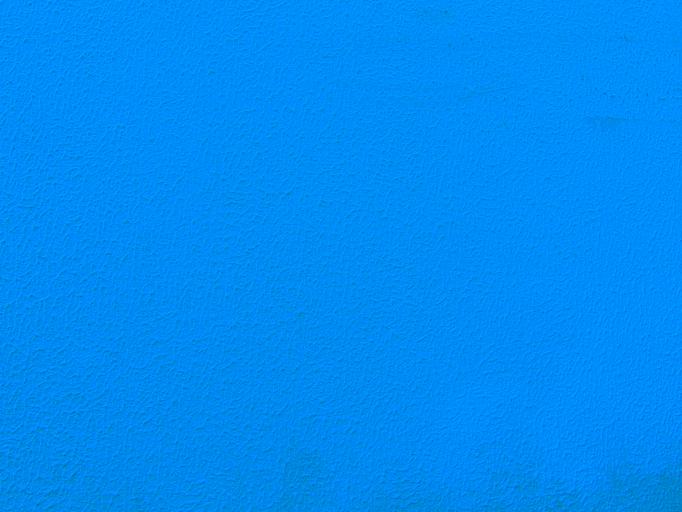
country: PT
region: Vila Real
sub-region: Peso da Regua
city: Peso da Regua
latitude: 41.1674
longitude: -7.7863
